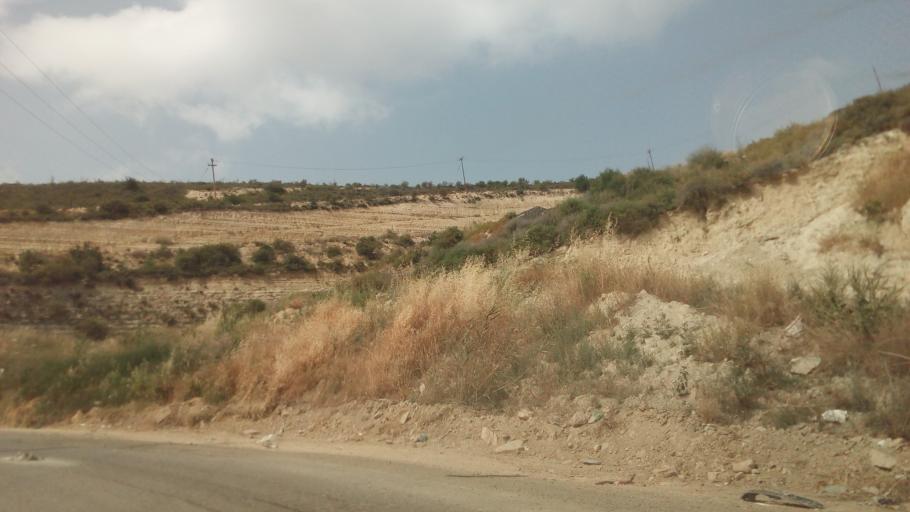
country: CY
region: Limassol
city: Pano Polemidia
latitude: 34.7451
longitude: 32.9524
